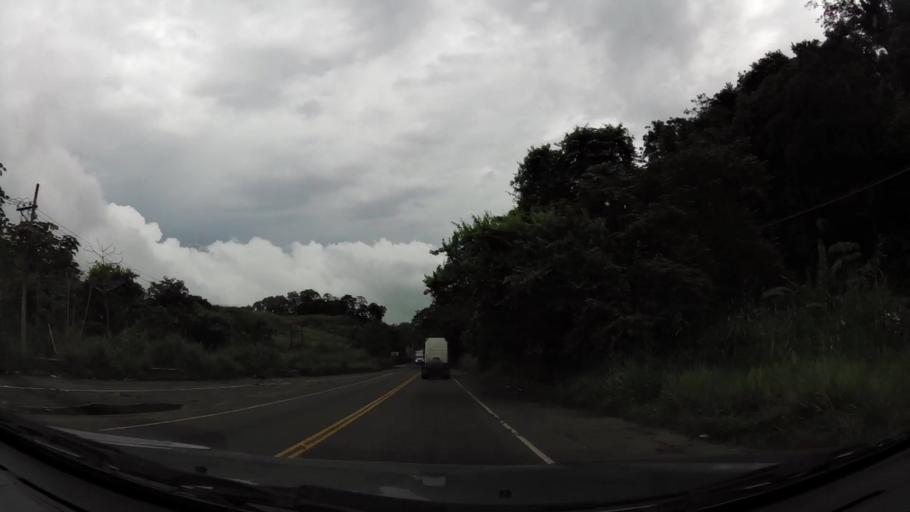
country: PA
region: Colon
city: Nuevo Vigia
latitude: 9.2185
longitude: -79.6263
